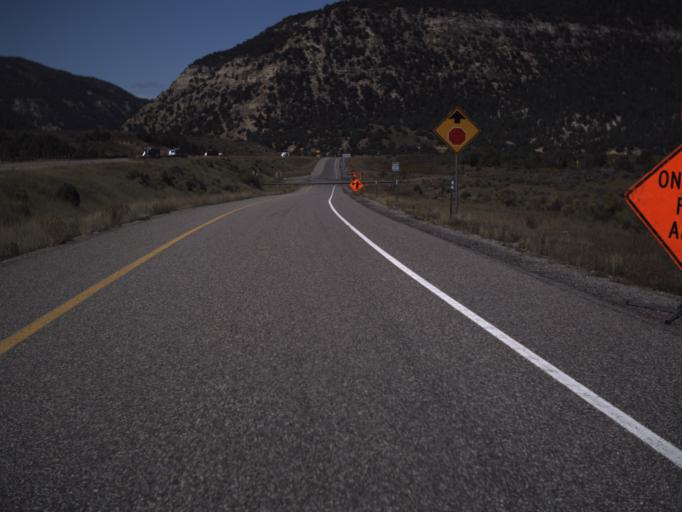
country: US
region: Utah
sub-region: Sevier County
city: Salina
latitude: 38.8782
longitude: -111.5612
